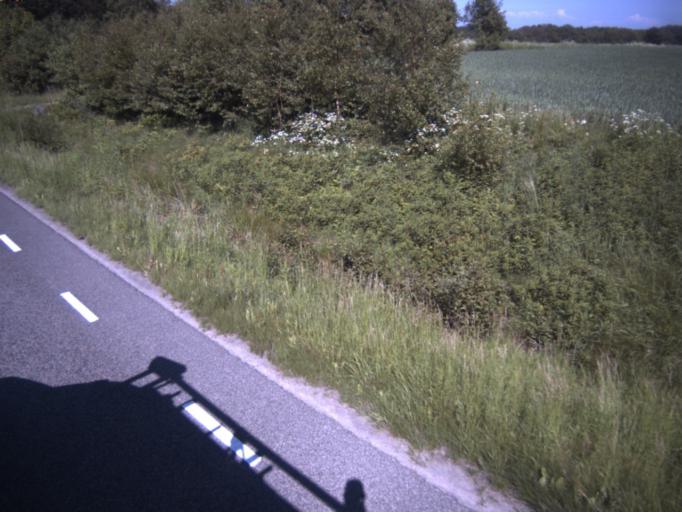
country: SE
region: Skane
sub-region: Helsingborg
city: Odakra
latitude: 56.0603
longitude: 12.7723
